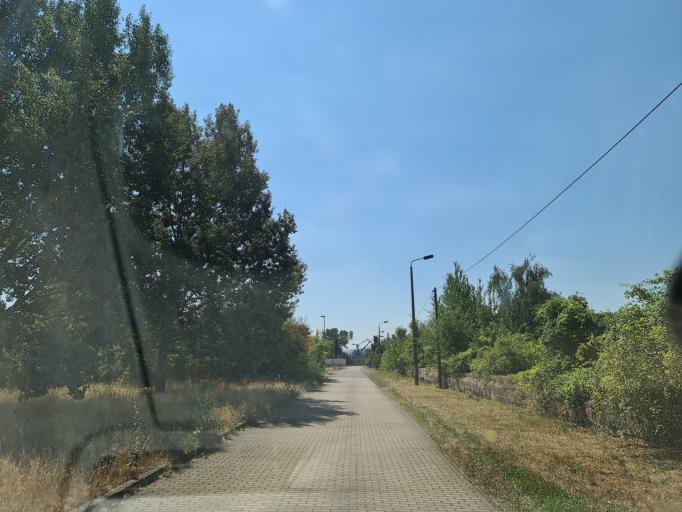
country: DE
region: Saxony
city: Dresden
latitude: 51.0705
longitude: 13.7107
